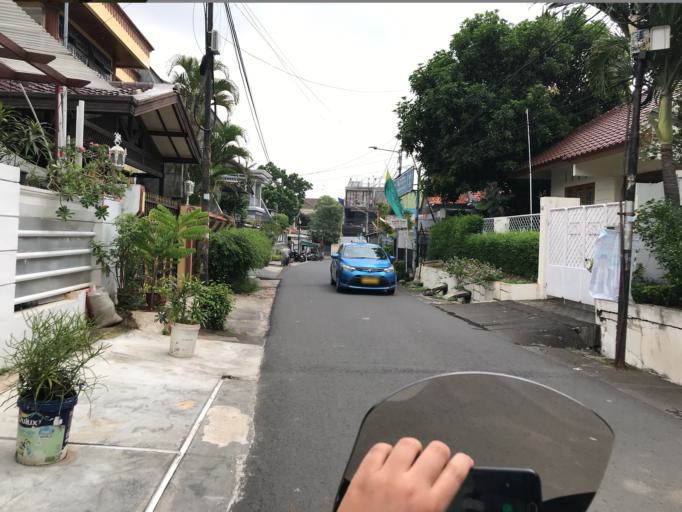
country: ID
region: Jakarta Raya
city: Jakarta
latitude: -6.2379
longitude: 106.8559
